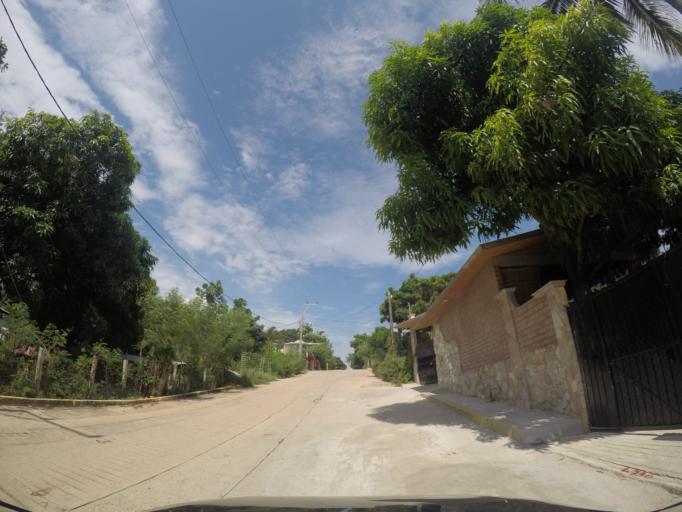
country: MX
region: Oaxaca
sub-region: Santa Maria Colotepec
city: Brisas de Zicatela
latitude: 15.8368
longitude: -97.0412
